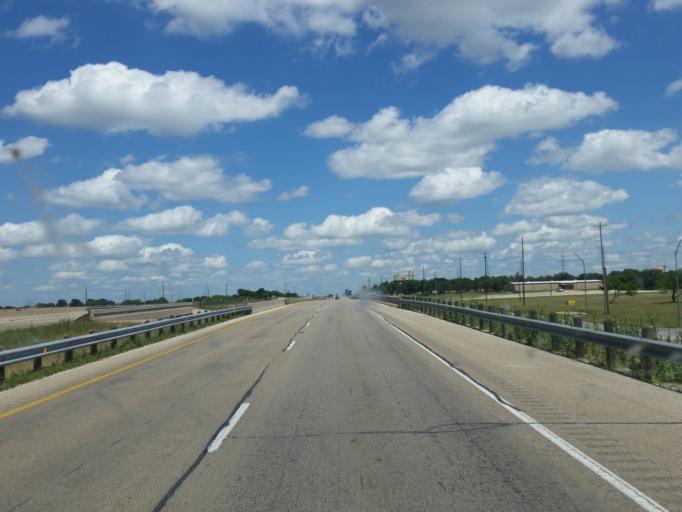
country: US
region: Texas
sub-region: Callahan County
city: Clyde
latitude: 32.4183
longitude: -99.5264
